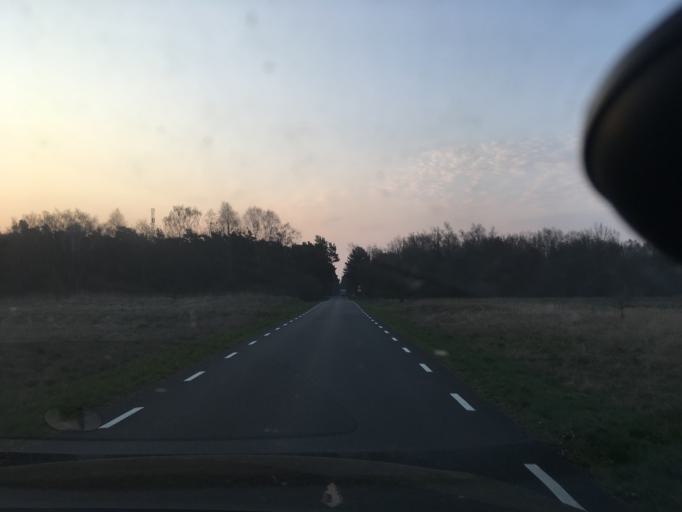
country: SE
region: Skane
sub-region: Simrishamns Kommun
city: Simrishamn
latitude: 55.3966
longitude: 14.1738
